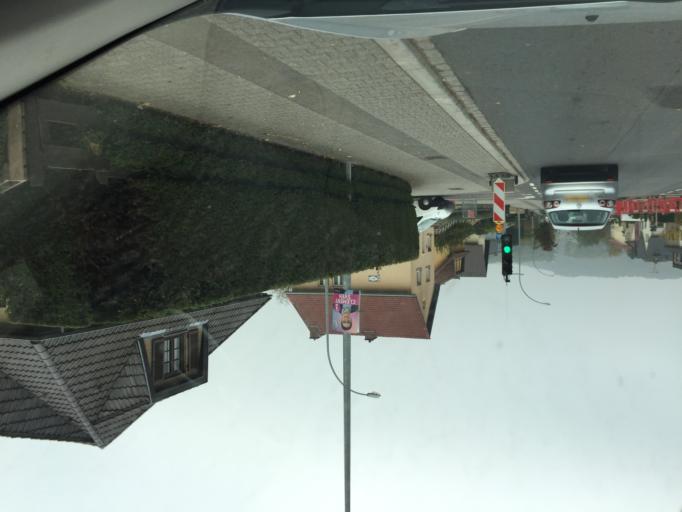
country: LU
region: Luxembourg
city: Moutfort
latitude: 49.5857
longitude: 6.2615
